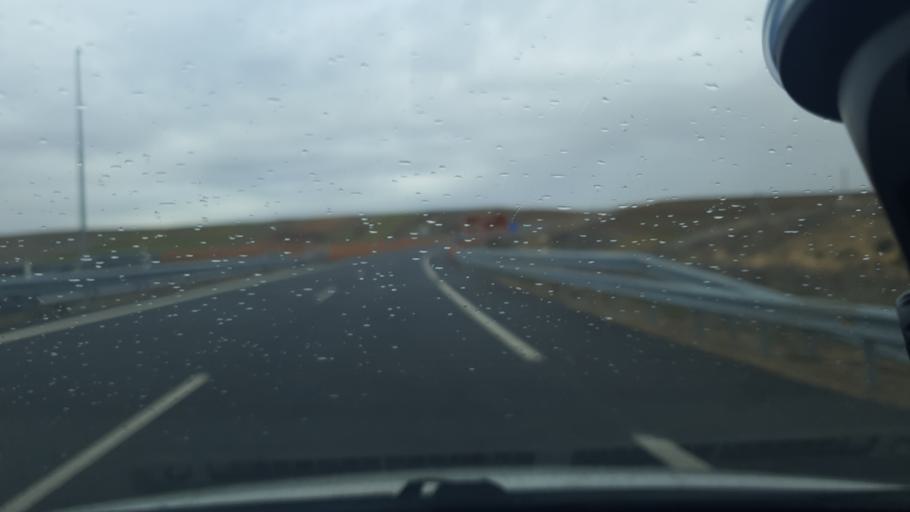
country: ES
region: Castille and Leon
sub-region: Provincia de Segovia
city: Roda de Eresma
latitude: 41.0223
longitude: -4.1869
